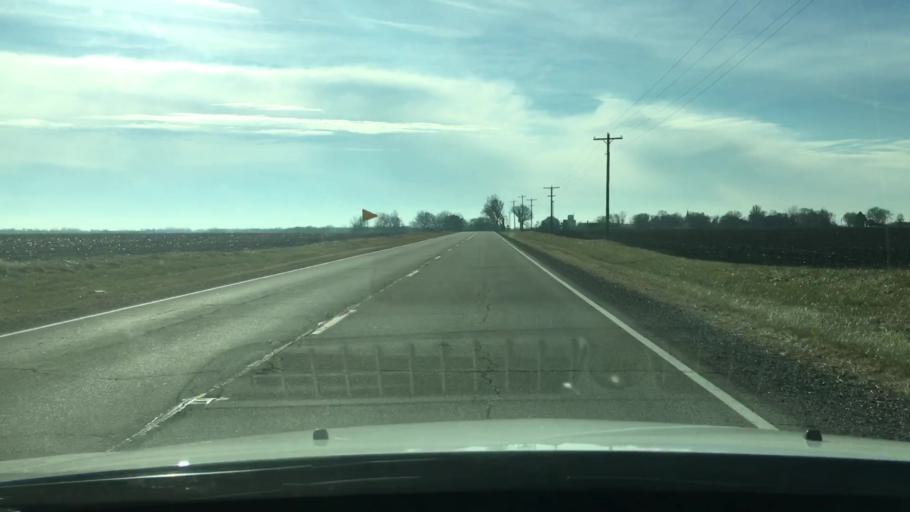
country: US
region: Illinois
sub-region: Woodford County
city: Washburn
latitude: 40.9913
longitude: -89.2339
